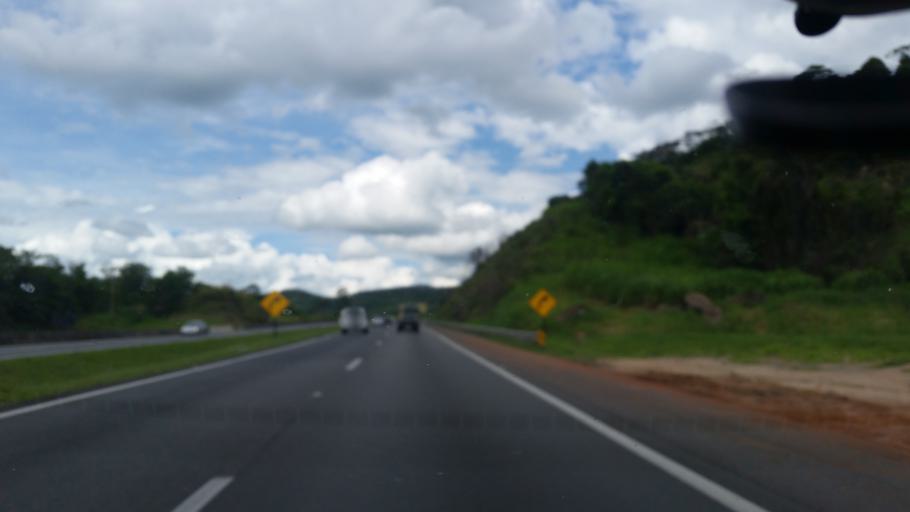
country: BR
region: Sao Paulo
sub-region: Valinhos
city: Valinhos
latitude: -22.9298
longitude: -46.9164
